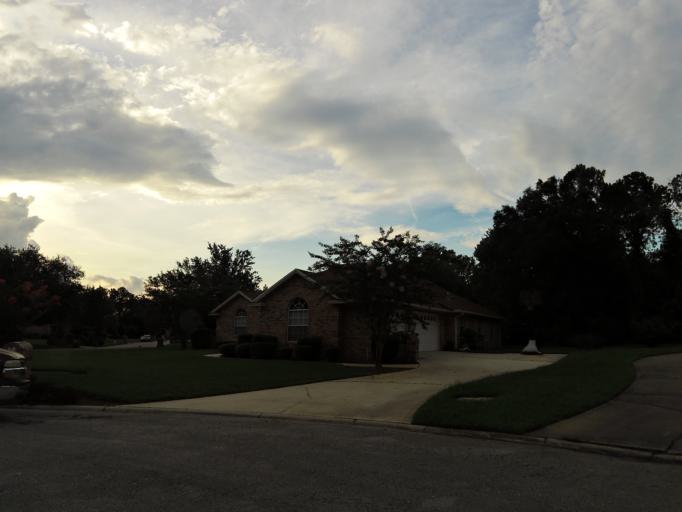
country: US
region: Florida
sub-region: Duval County
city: Baldwin
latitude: 30.3089
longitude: -81.8265
